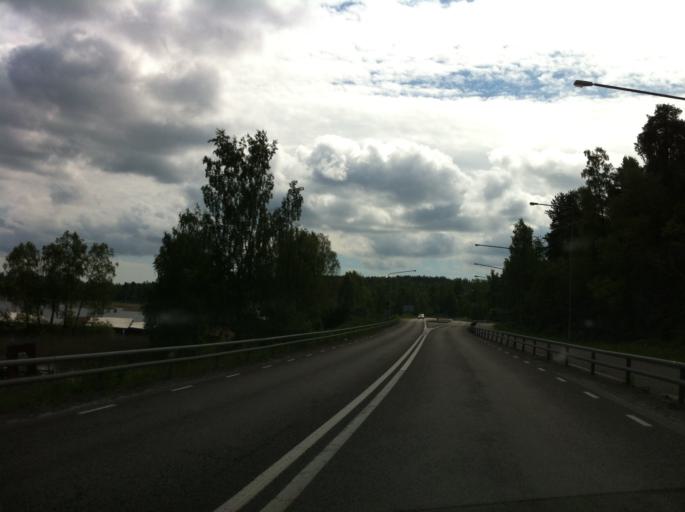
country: SE
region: Vaermland
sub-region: Grums Kommun
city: Slottsbron
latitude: 59.3308
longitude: 13.1018
